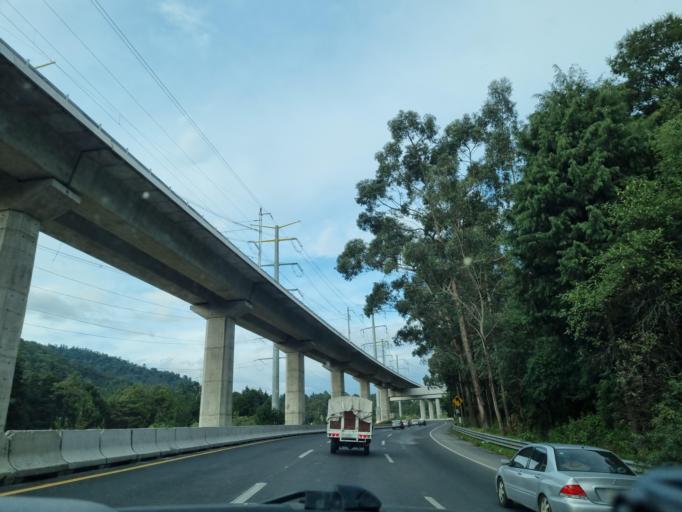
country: MX
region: Morelos
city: San Jeronimo Acazulco
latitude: 19.2958
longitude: -99.4158
